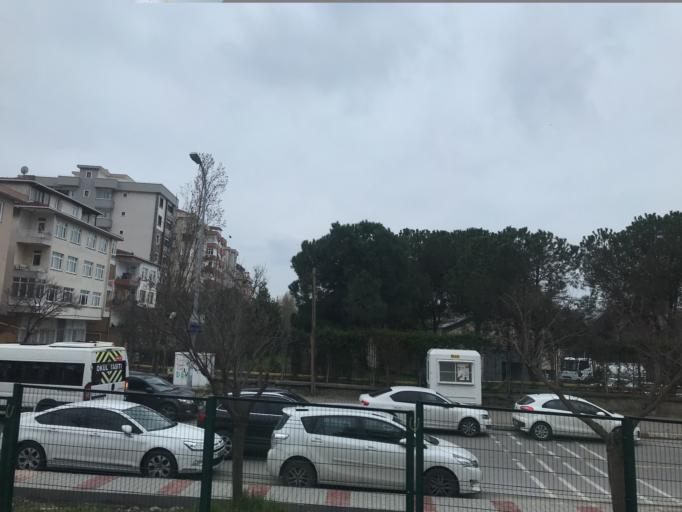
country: TR
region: Istanbul
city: Maltepe
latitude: 40.9064
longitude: 29.1600
